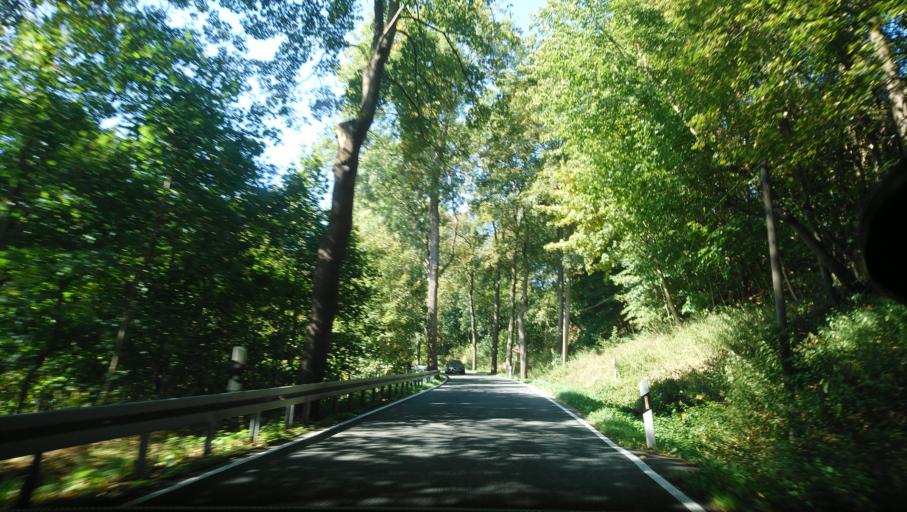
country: DE
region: Saxony
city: Barenstein
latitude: 50.5110
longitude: 13.0334
